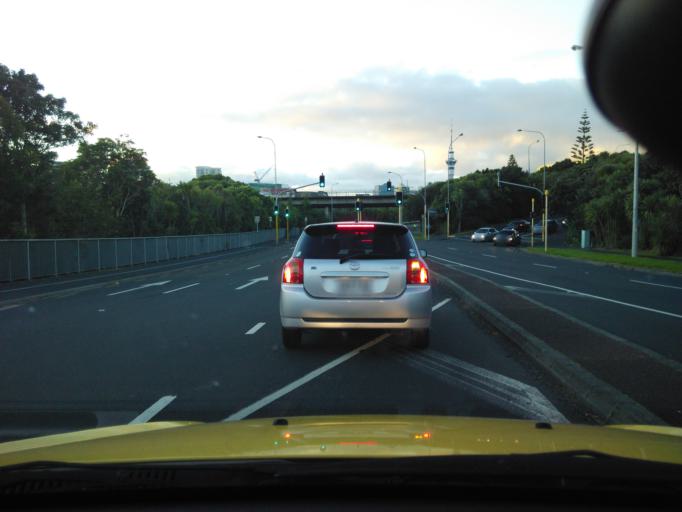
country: NZ
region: Auckland
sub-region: Auckland
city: Auckland
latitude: -36.8641
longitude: 174.7550
